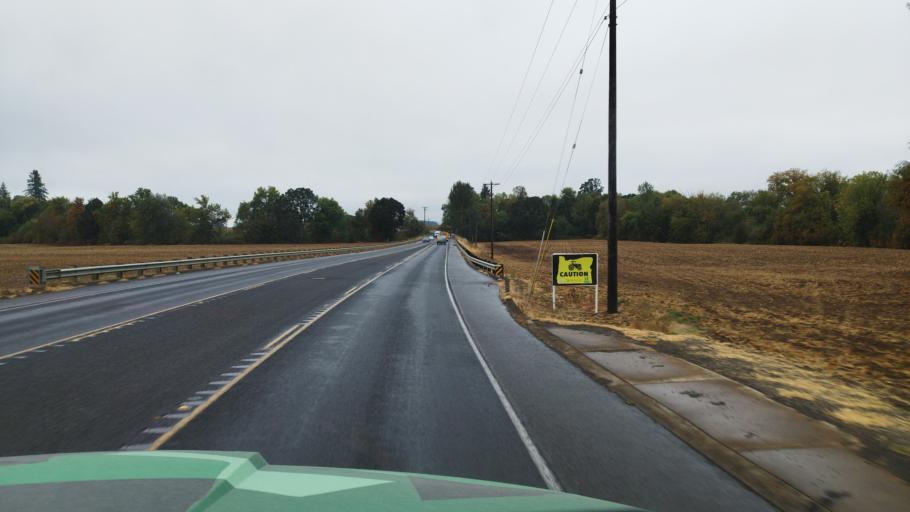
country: US
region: Oregon
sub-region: Washington County
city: Cornelius
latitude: 45.5569
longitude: -123.0602
